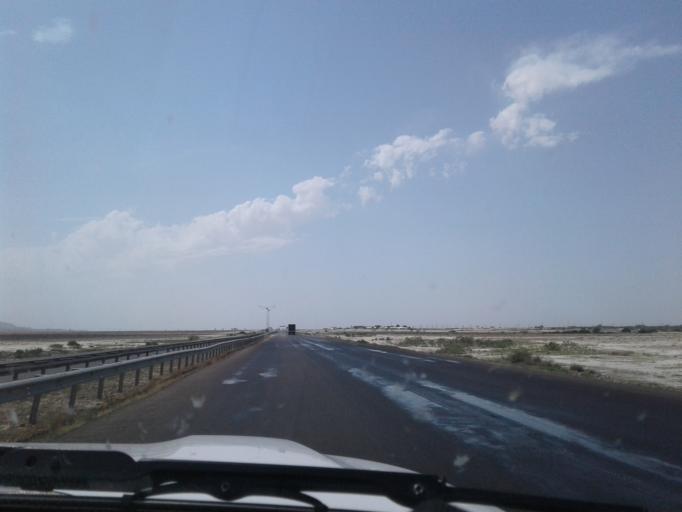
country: IR
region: Razavi Khorasan
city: Dargaz
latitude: 37.7110
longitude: 59.0260
